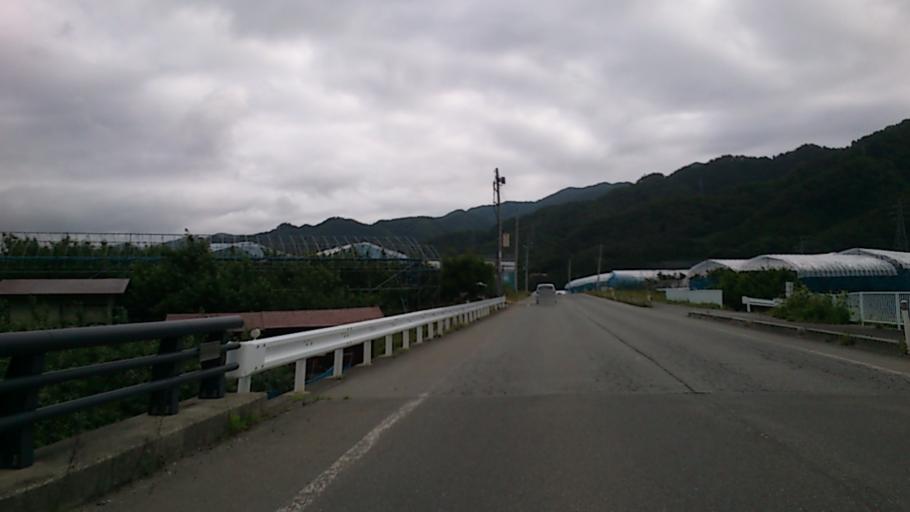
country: JP
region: Yamagata
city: Tendo
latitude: 38.3111
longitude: 140.4081
